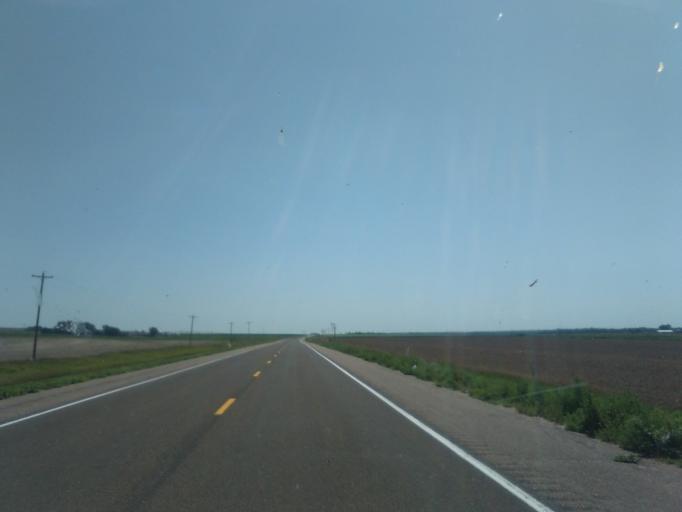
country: US
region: Nebraska
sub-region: Dundy County
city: Benkelman
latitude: 40.1256
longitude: -101.3528
